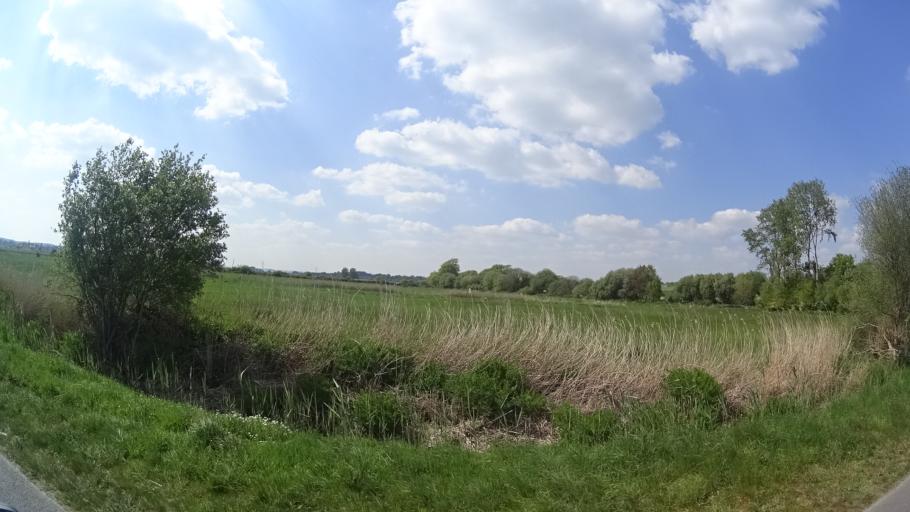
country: FR
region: Brittany
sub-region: Departement du Morbihan
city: Rieux
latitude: 47.5851
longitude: -2.1110
